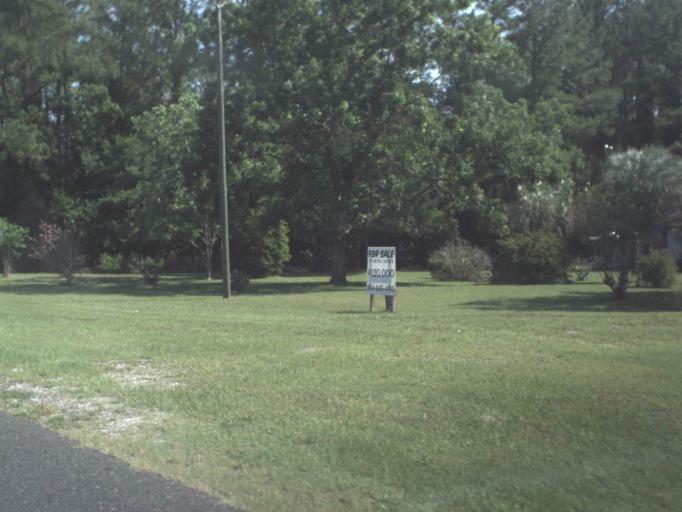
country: US
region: Florida
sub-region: Nassau County
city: Hilliard
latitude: 30.7172
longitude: -81.9358
